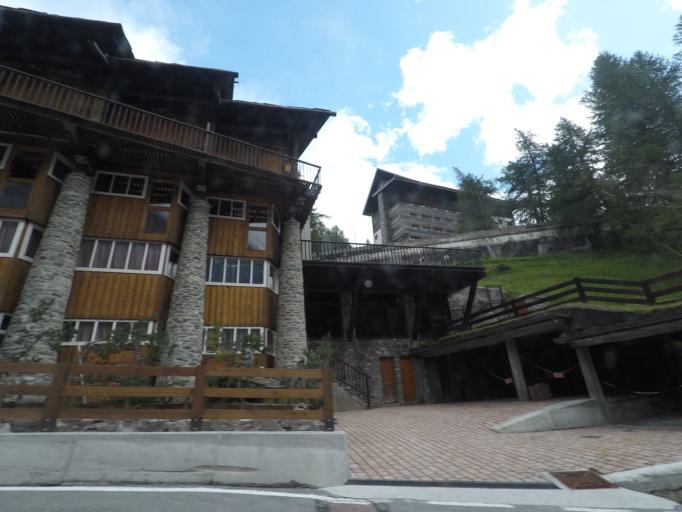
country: IT
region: Aosta Valley
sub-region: Valle d'Aosta
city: Paquier
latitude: 45.9337
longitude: 7.6317
